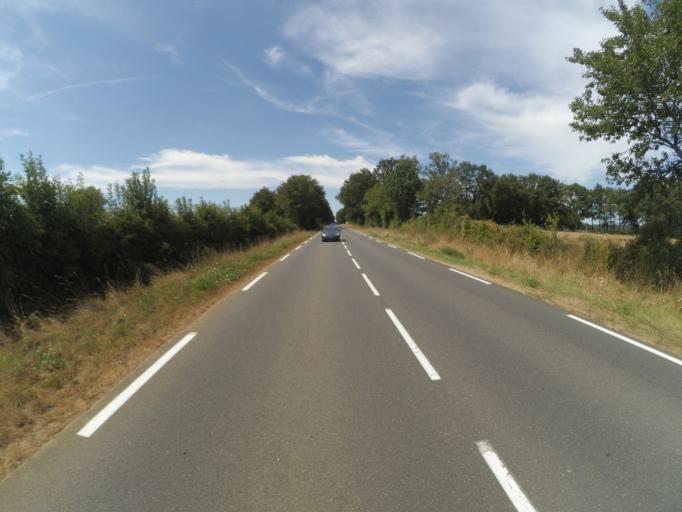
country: FR
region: Poitou-Charentes
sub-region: Departement de la Charente
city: Confolens
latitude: 45.9543
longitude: 0.7086
